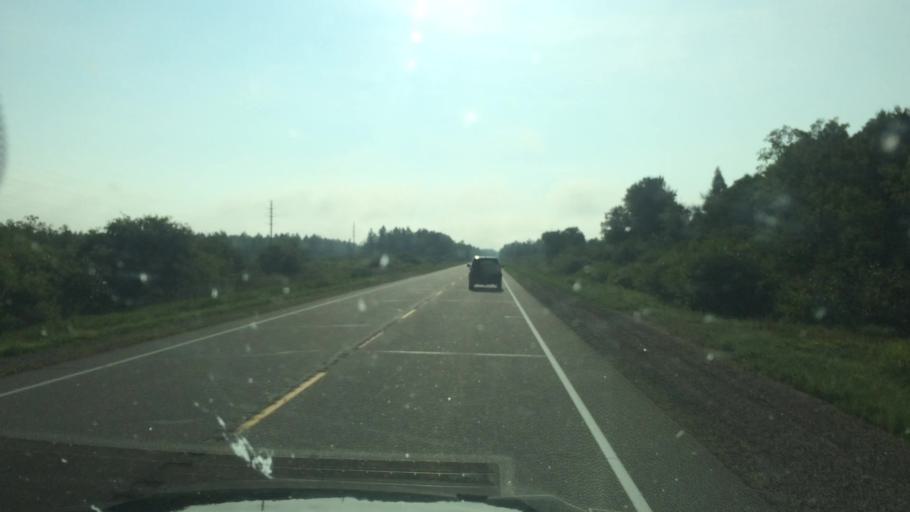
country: US
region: Wisconsin
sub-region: Langlade County
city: Antigo
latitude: 45.1465
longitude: -89.3386
